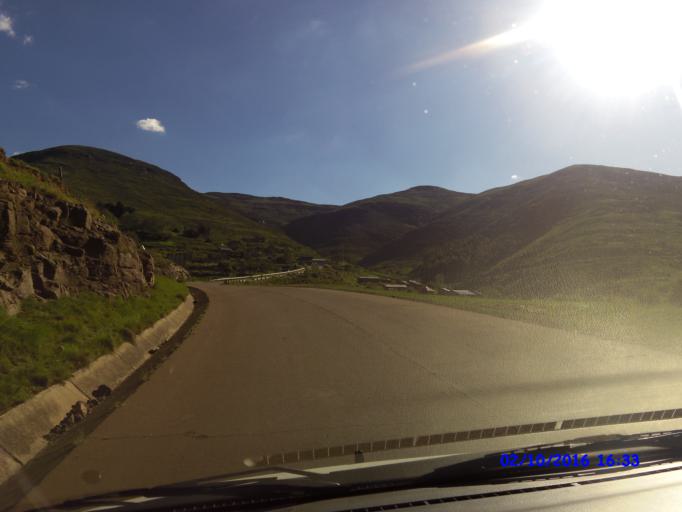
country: LS
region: Maseru
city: Nako
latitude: -29.4915
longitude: 28.0617
